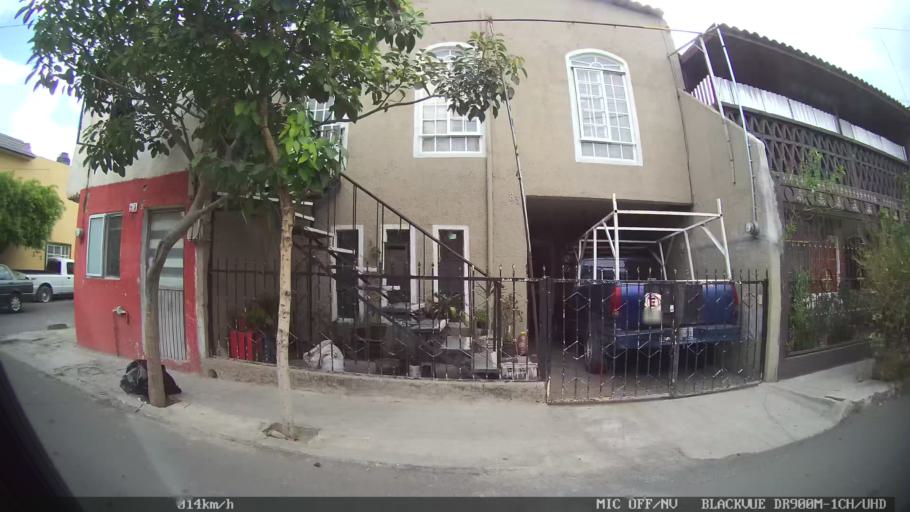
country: MX
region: Jalisco
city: Tlaquepaque
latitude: 20.6295
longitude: -103.2721
